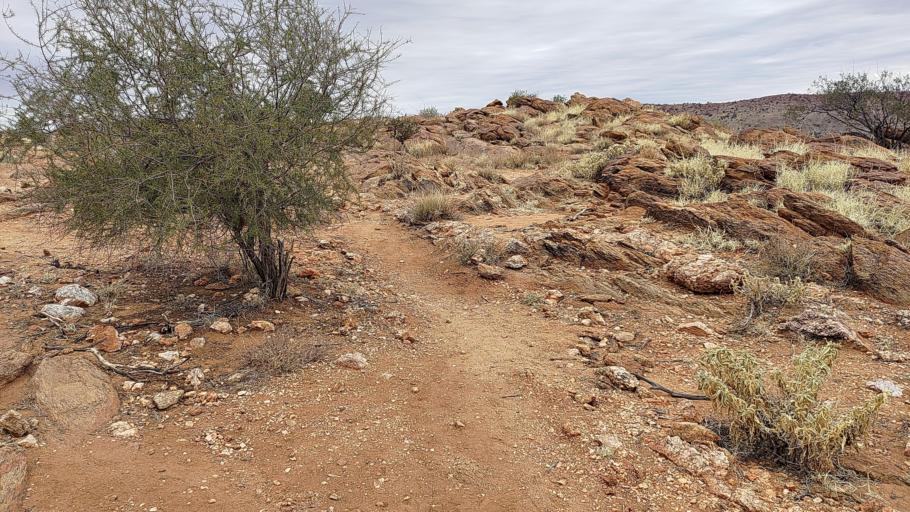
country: AU
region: Northern Territory
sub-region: Alice Springs
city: Alice Springs
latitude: -23.7047
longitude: 133.8851
